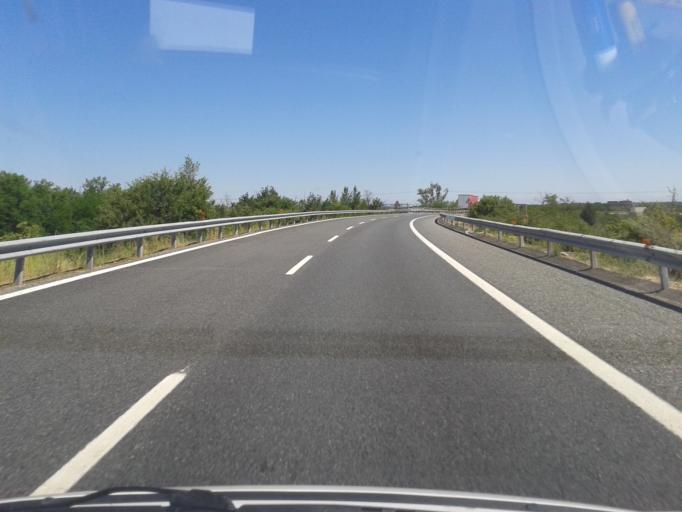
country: IT
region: Piedmont
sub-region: Provincia di Alessandria
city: Predosa
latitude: 44.7604
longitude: 8.6456
